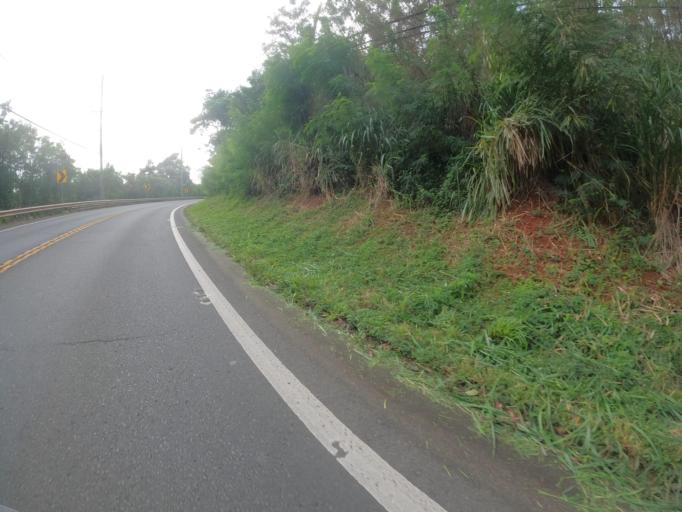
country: US
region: Hawaii
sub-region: Honolulu County
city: Kahalu'u
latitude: 21.4785
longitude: -157.8432
